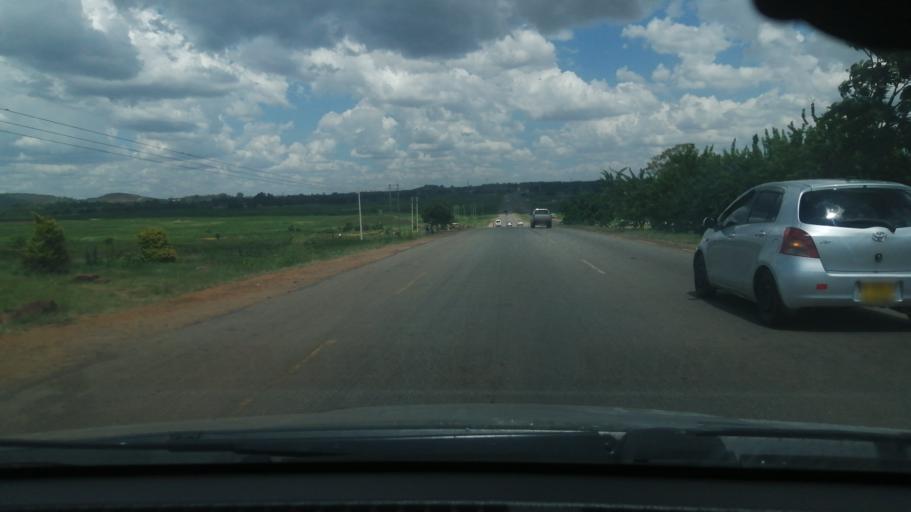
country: ZW
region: Harare
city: Harare
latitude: -17.8197
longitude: 30.9011
